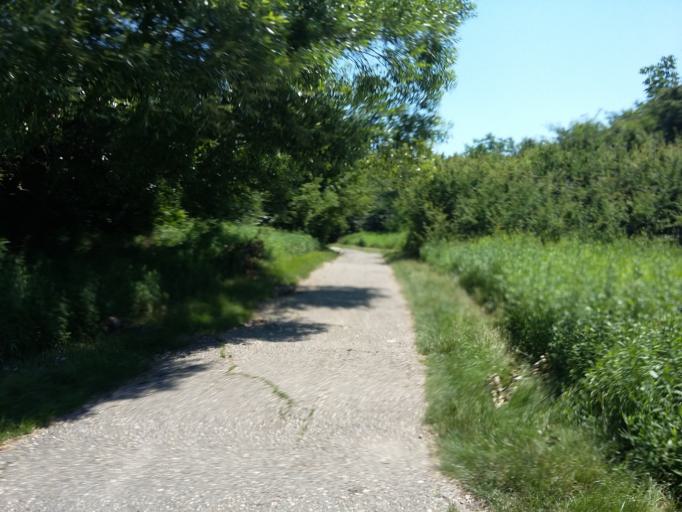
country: AT
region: Lower Austria
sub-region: Politischer Bezirk Bruck an der Leitha
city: Hainburg an der Donau
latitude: 48.2115
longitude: 16.9678
